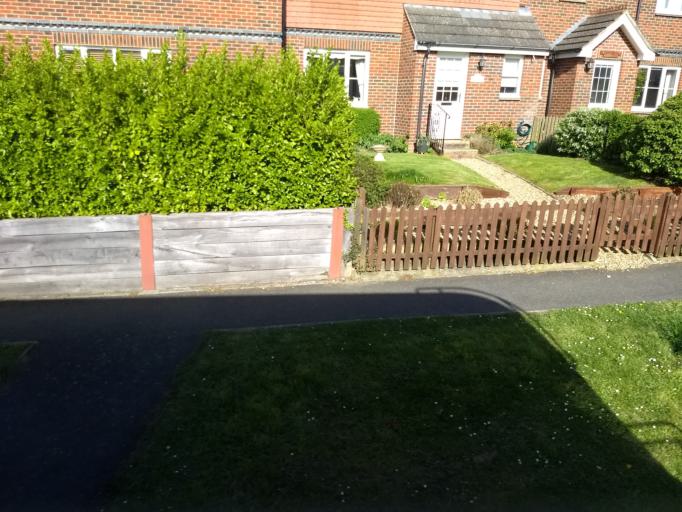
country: GB
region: England
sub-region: Isle of Wight
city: Bembridge
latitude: 50.6920
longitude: -1.0910
